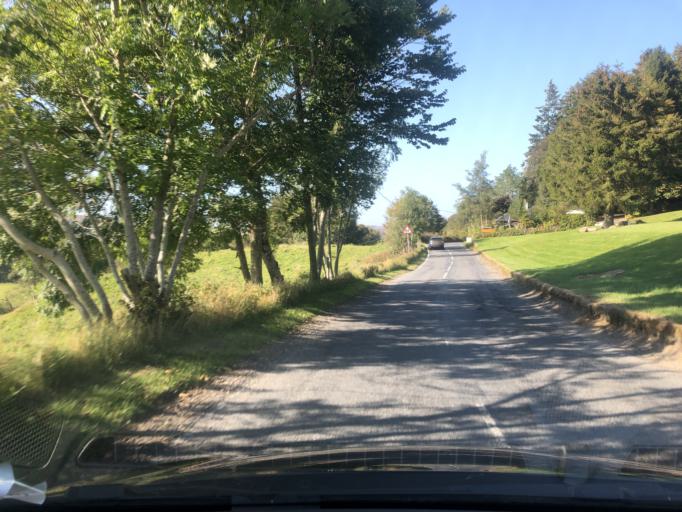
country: GB
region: Scotland
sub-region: Perth and Kinross
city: Blairgowrie
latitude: 56.6756
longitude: -3.4642
